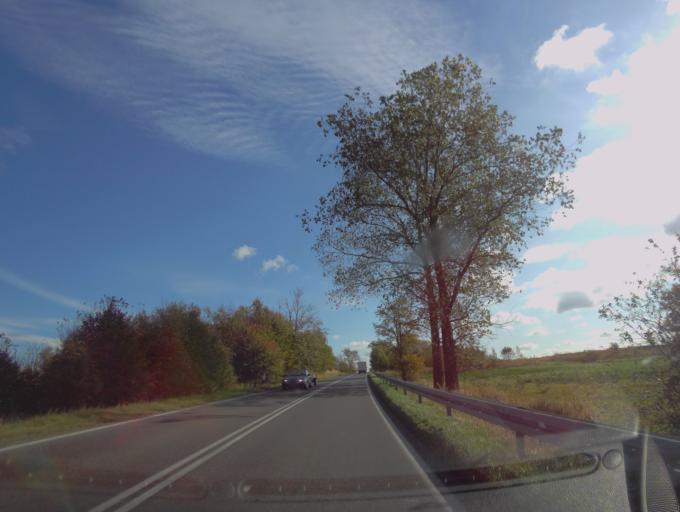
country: PL
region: Subcarpathian Voivodeship
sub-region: Powiat rzeszowski
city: Wolka Niedzwiedzka
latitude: 50.2451
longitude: 22.1966
